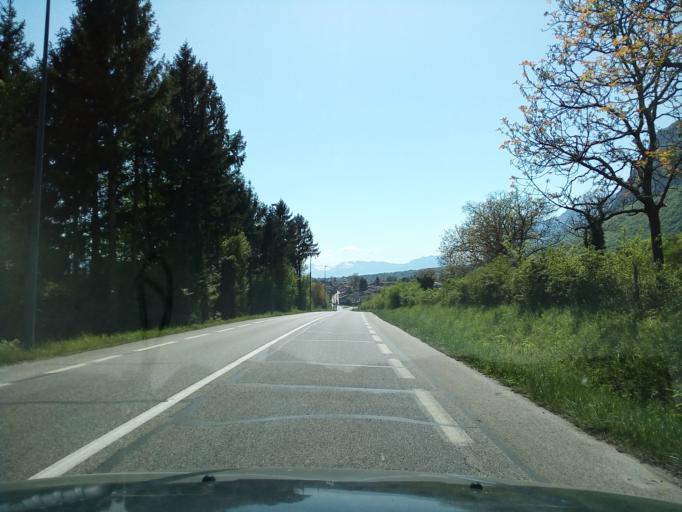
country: FR
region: Rhone-Alpes
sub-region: Departement de l'Isere
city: Saint-Hilaire
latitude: 45.2923
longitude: 5.8933
